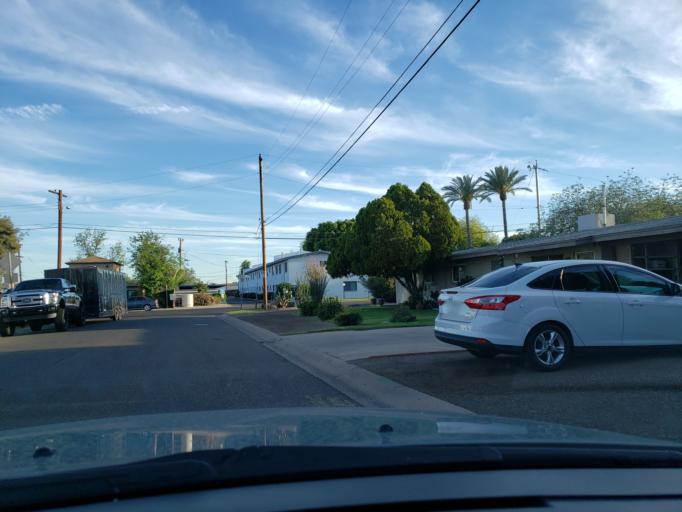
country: US
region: Arizona
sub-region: Maricopa County
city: Phoenix
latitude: 33.5206
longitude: -112.0629
